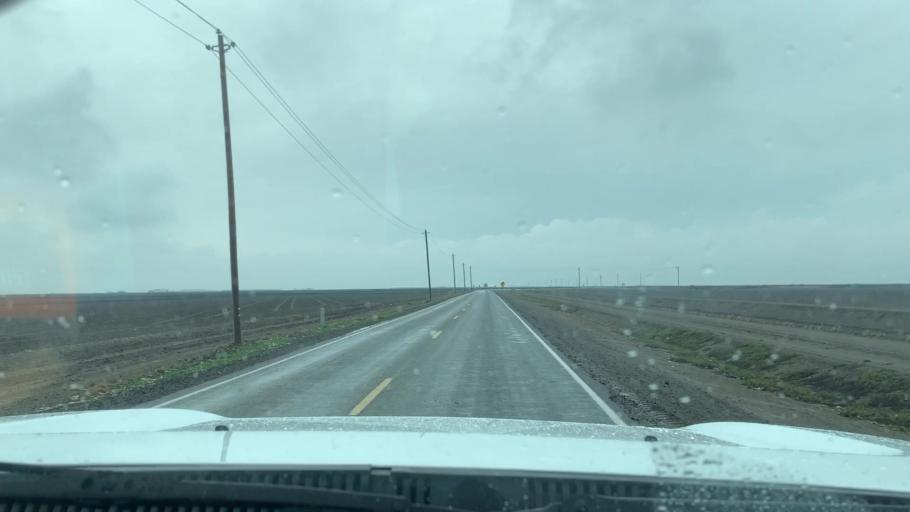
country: US
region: California
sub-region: Tulare County
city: Alpaugh
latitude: 35.9665
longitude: -119.5720
